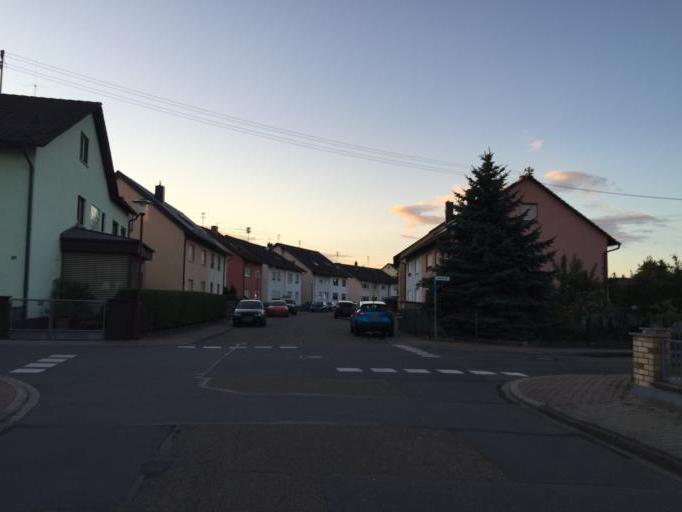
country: DE
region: Baden-Wuerttemberg
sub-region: Karlsruhe Region
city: Oftersheim
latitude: 49.3703
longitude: 8.5784
